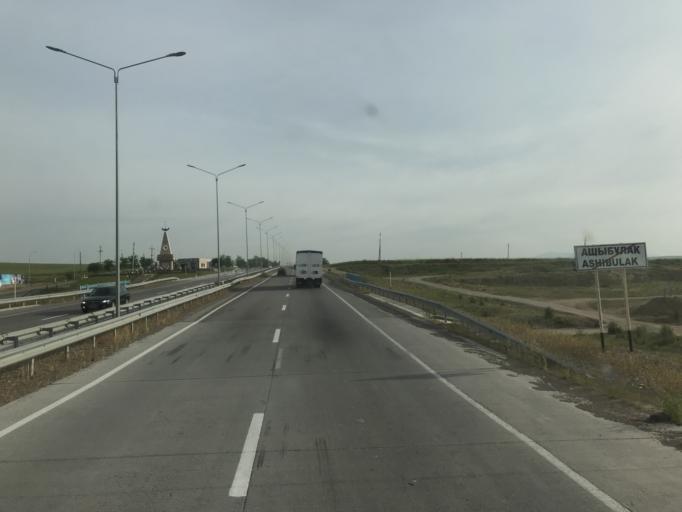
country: KZ
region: Ongtustik Qazaqstan
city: Qazyqurt
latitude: 41.8019
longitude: 69.3947
